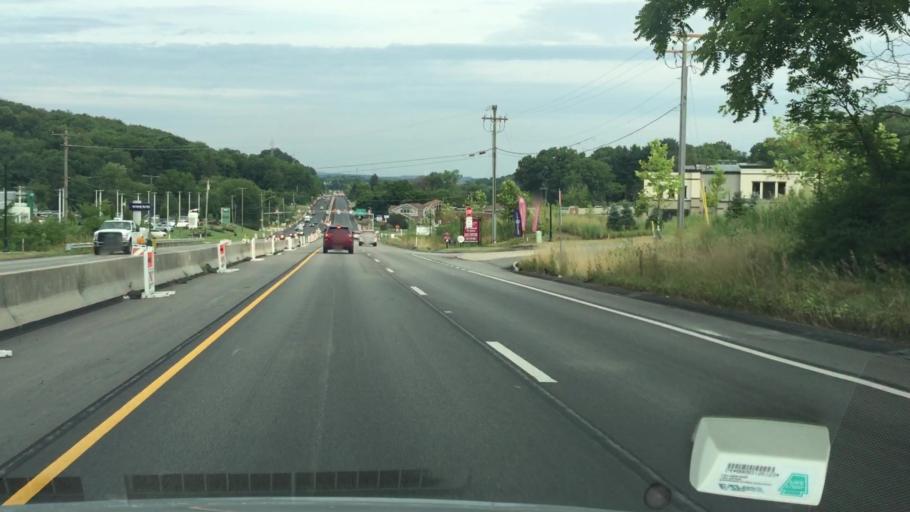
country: US
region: Pennsylvania
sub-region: Allegheny County
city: Bradford Woods
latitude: 40.6485
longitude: -80.0760
